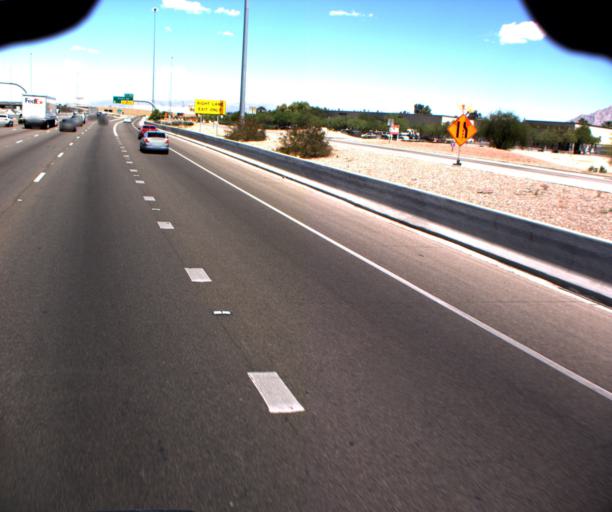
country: US
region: Arizona
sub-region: Pima County
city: Flowing Wells
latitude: 32.2651
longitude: -111.0067
